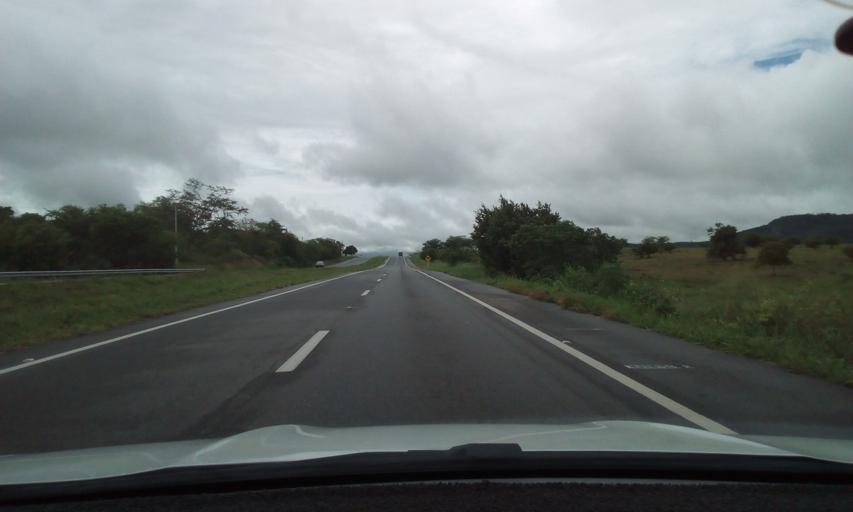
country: BR
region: Paraiba
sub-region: Gurinhem
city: Gurinhem
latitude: -7.1927
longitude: -35.4776
